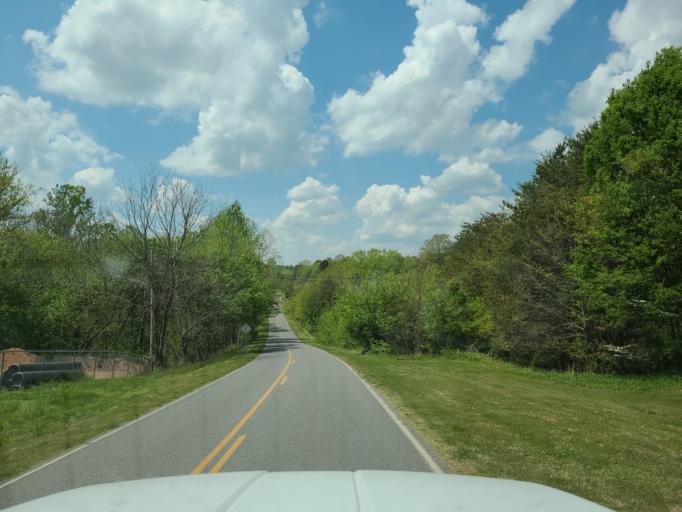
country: US
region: North Carolina
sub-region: Cleveland County
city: Shelby
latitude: 35.3283
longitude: -81.4709
